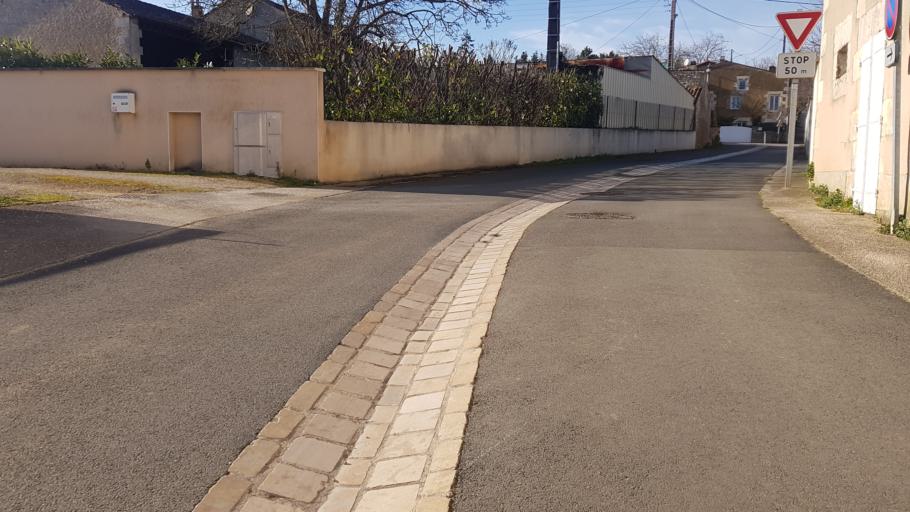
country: FR
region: Poitou-Charentes
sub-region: Departement de la Vienne
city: Migne-Auxances
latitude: 46.6351
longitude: 0.3351
